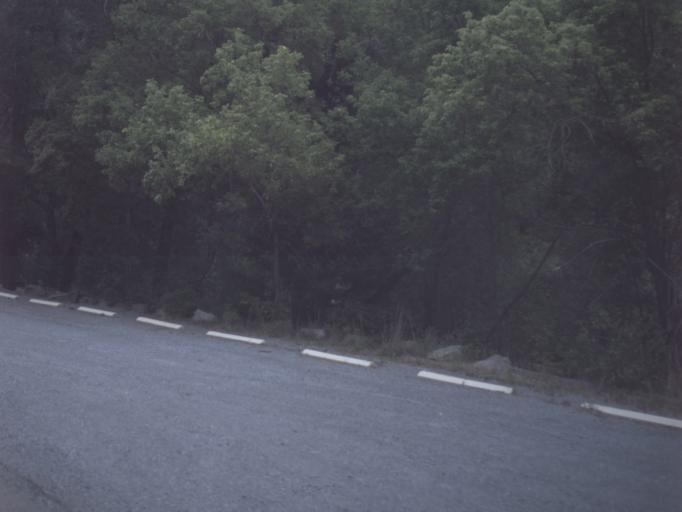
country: US
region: Utah
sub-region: Utah County
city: Cedar Hills
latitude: 40.4439
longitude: -111.7040
